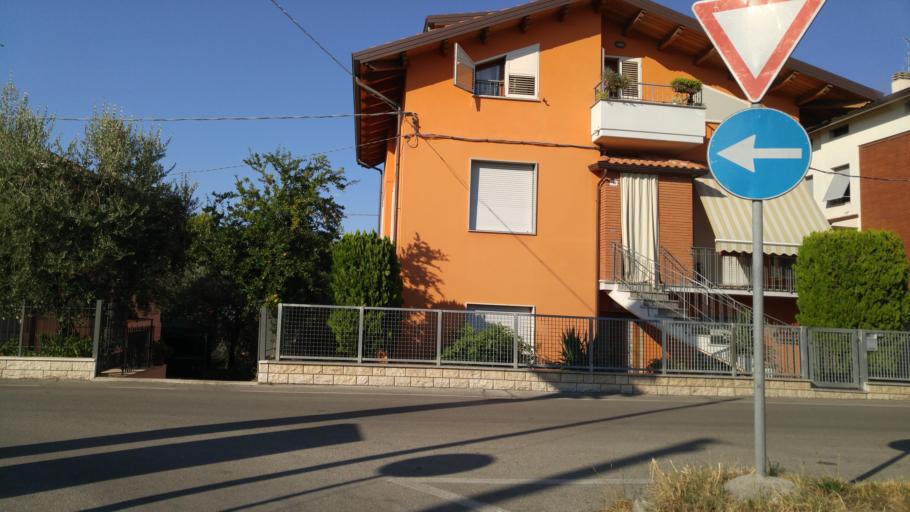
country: IT
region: The Marches
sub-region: Provincia di Pesaro e Urbino
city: Villa Ceccolini
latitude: 43.8822
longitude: 12.8652
